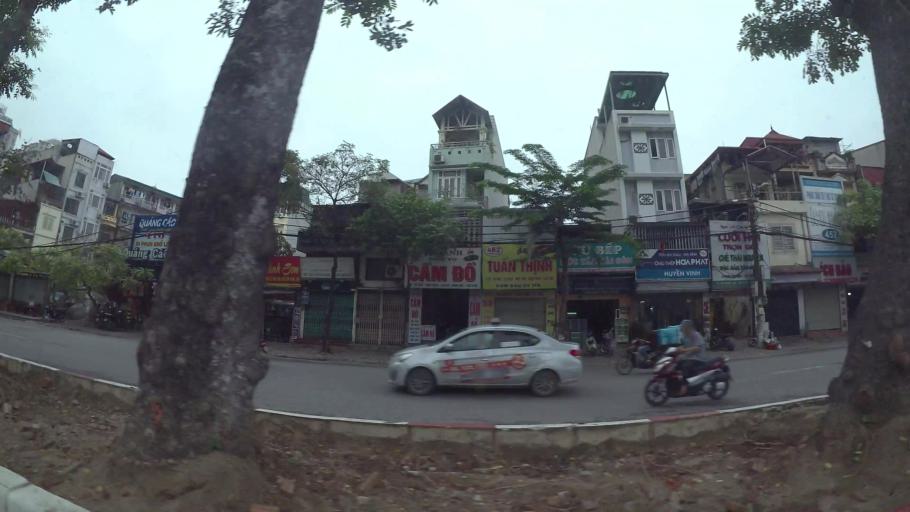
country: VN
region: Ha Noi
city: Thanh Xuan
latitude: 21.0096
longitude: 105.8130
